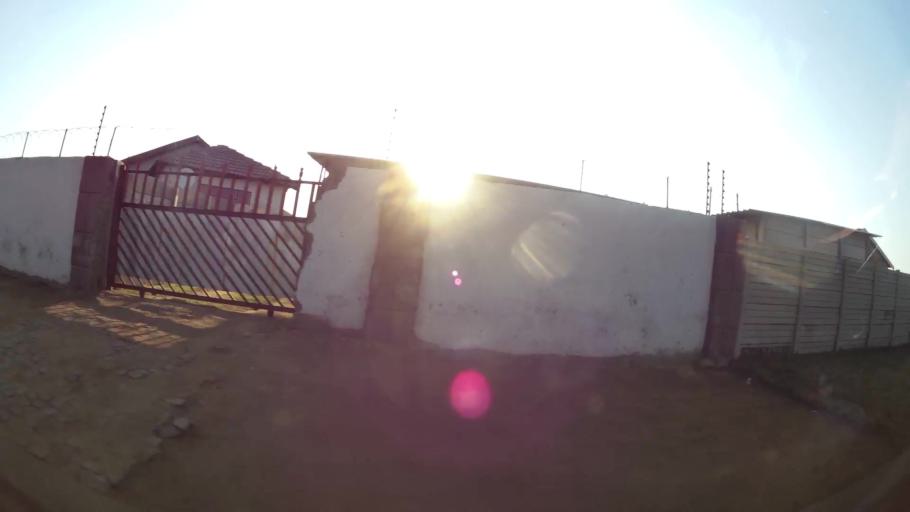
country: ZA
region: Gauteng
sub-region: Ekurhuleni Metropolitan Municipality
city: Benoni
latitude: -26.1239
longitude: 28.3791
